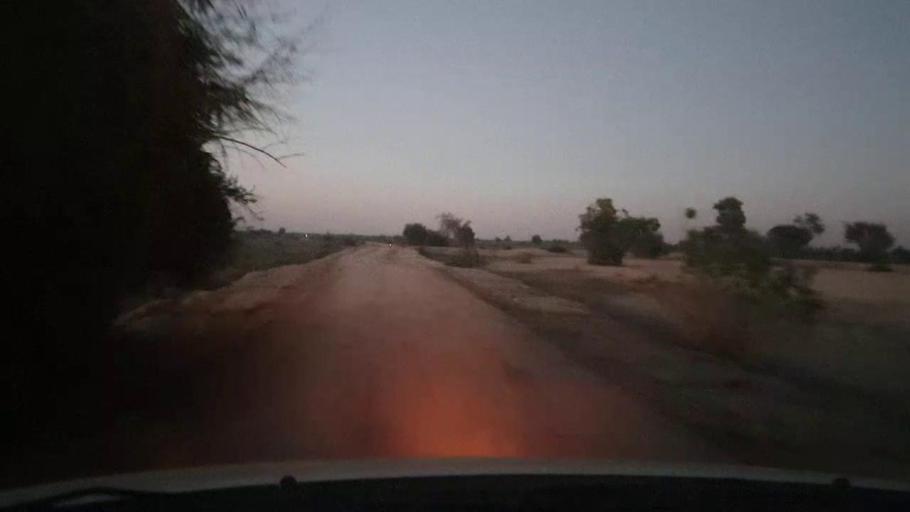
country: PK
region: Sindh
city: Phulji
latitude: 26.9048
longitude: 67.4707
